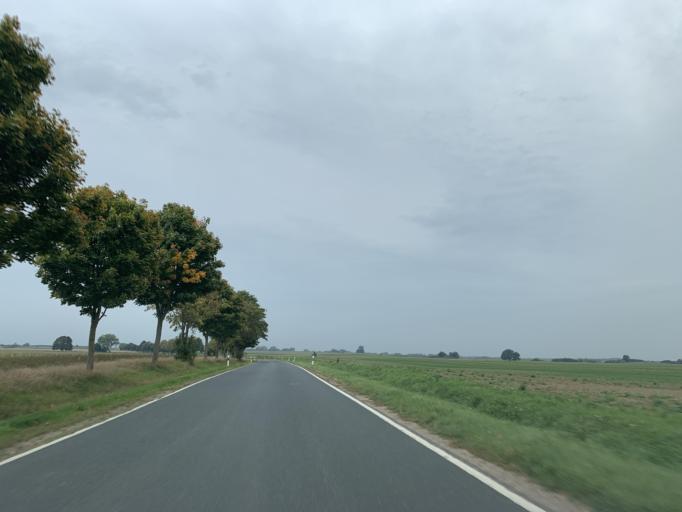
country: DE
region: Mecklenburg-Vorpommern
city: Woldegk
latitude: 53.3283
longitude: 13.5614
